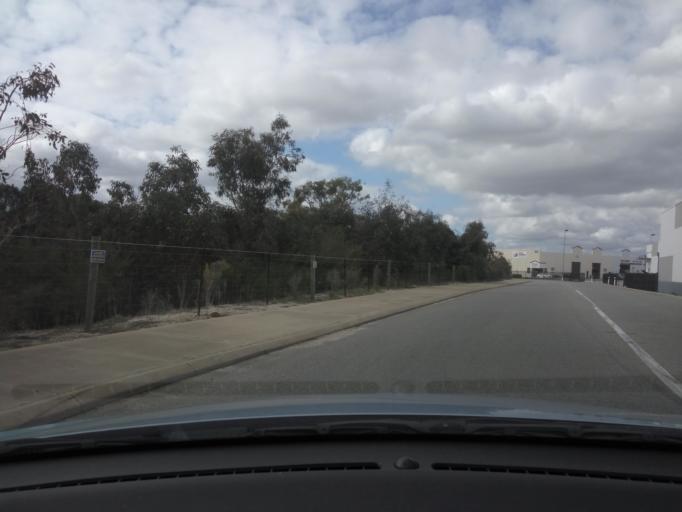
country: AU
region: Western Australia
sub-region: City of Cockburn
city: Success
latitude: -32.1244
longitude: 115.8701
